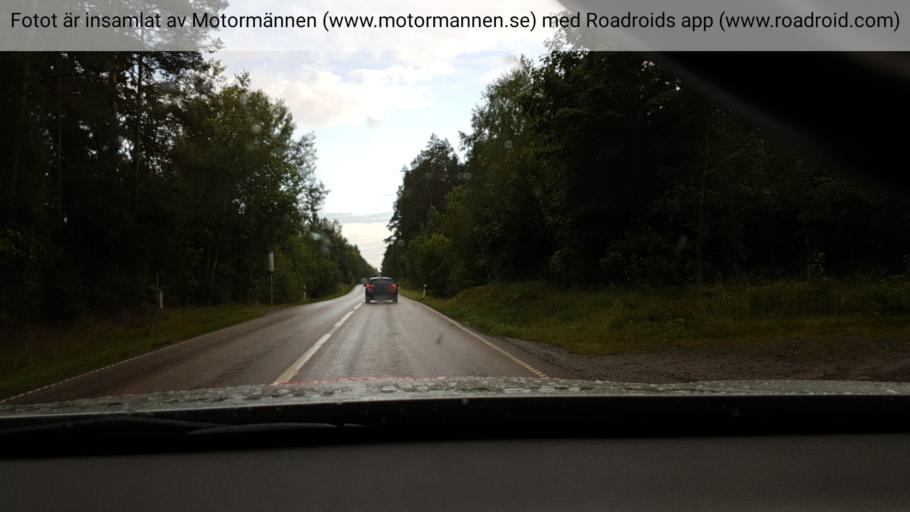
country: SE
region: Stockholm
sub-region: Norrtalje Kommun
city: Norrtalje
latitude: 59.8693
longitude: 18.6956
